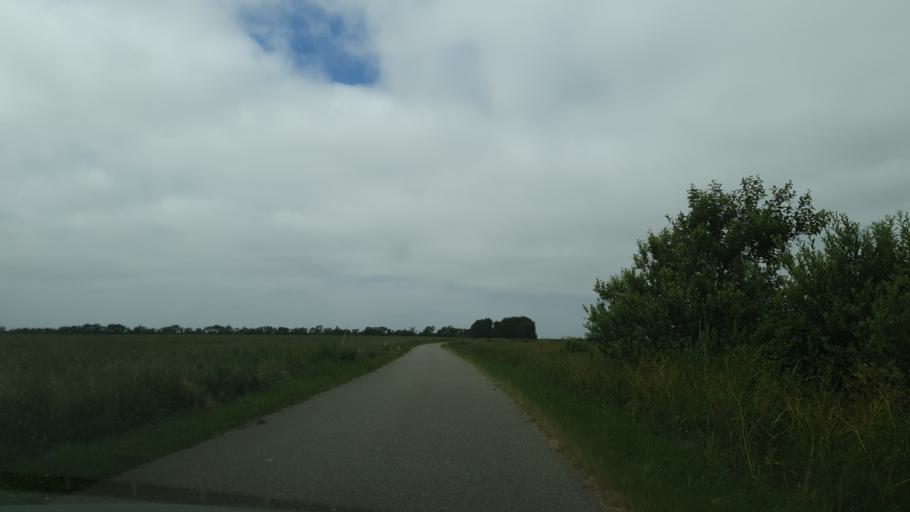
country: DK
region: Central Jutland
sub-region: Ringkobing-Skjern Kommune
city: Skjern
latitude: 55.9208
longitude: 8.4052
